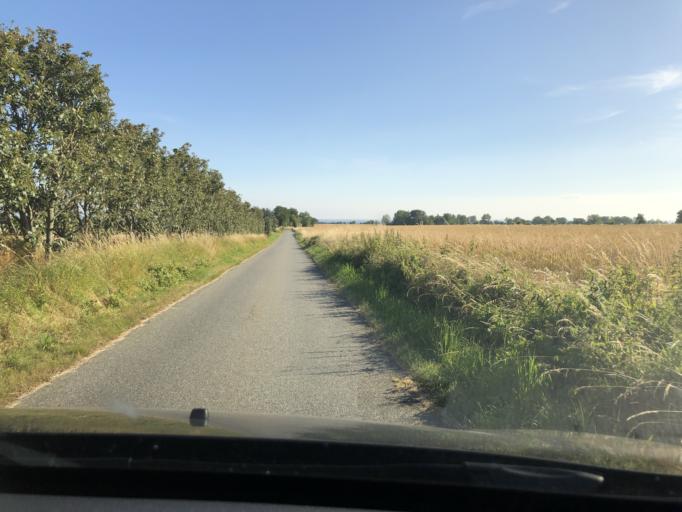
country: DK
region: South Denmark
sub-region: AEro Kommune
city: AEroskobing
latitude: 54.8594
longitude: 10.3805
